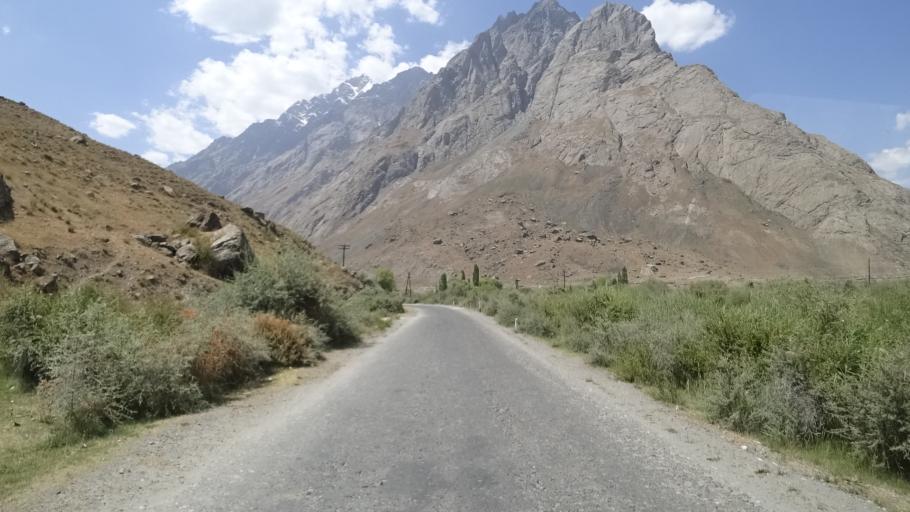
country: TJ
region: Gorno-Badakhshan
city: Rushon
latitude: 37.9228
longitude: 71.5978
